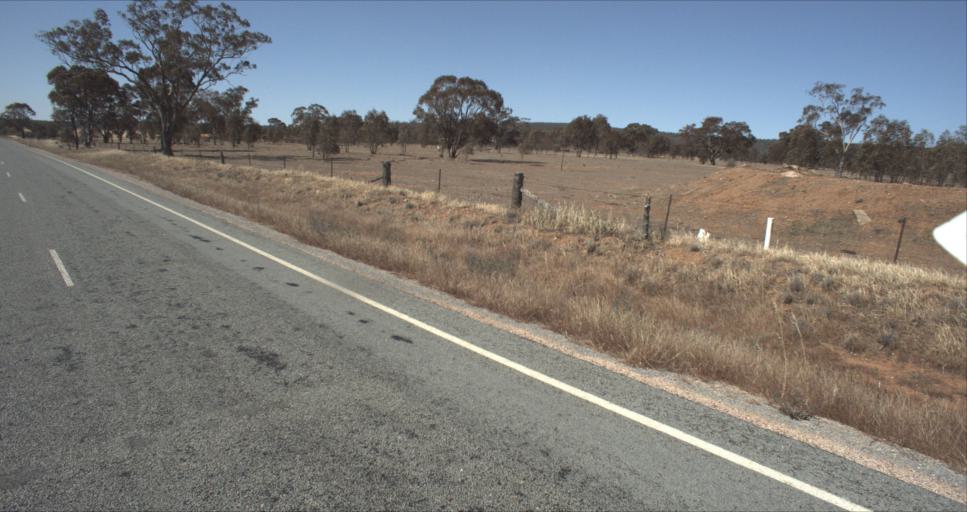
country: AU
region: New South Wales
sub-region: Leeton
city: Leeton
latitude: -34.4618
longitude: 146.4376
